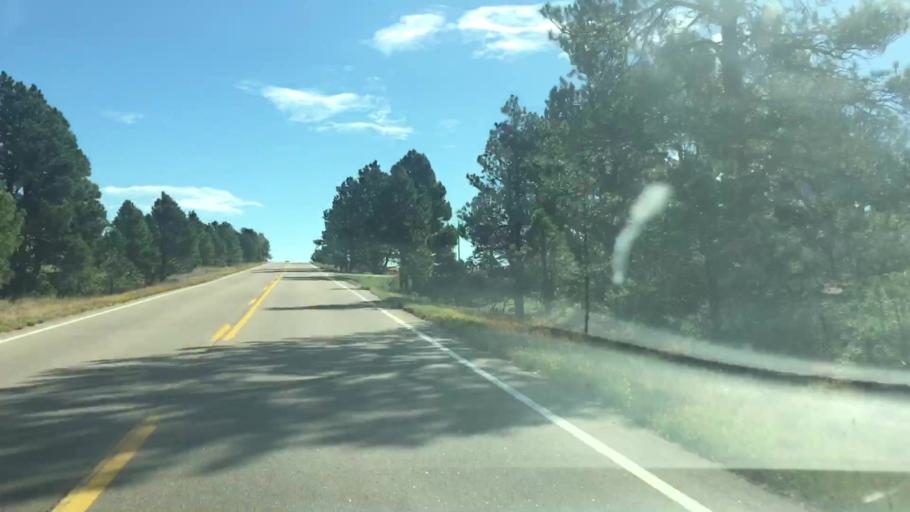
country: US
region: Colorado
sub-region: Elbert County
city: Kiowa
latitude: 39.2736
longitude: -104.1901
